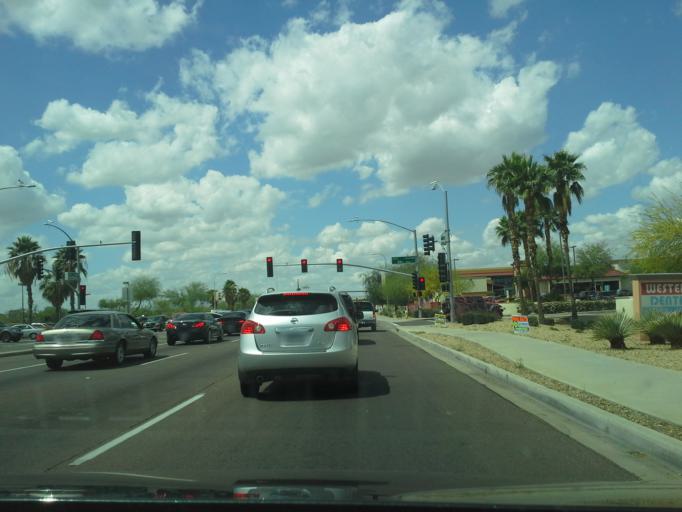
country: US
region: Arizona
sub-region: Maricopa County
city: Peoria
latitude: 33.6101
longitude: -112.2396
